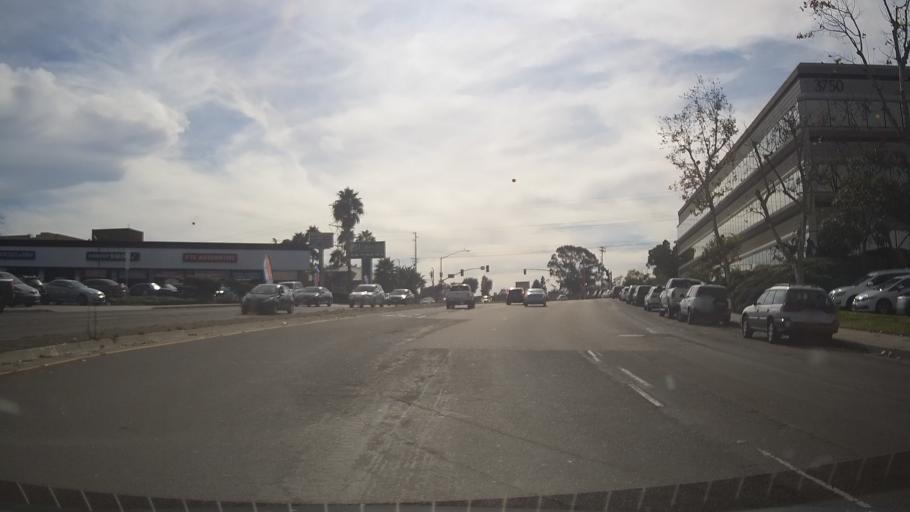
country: US
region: California
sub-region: San Diego County
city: San Diego
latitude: 32.8128
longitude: -117.1531
